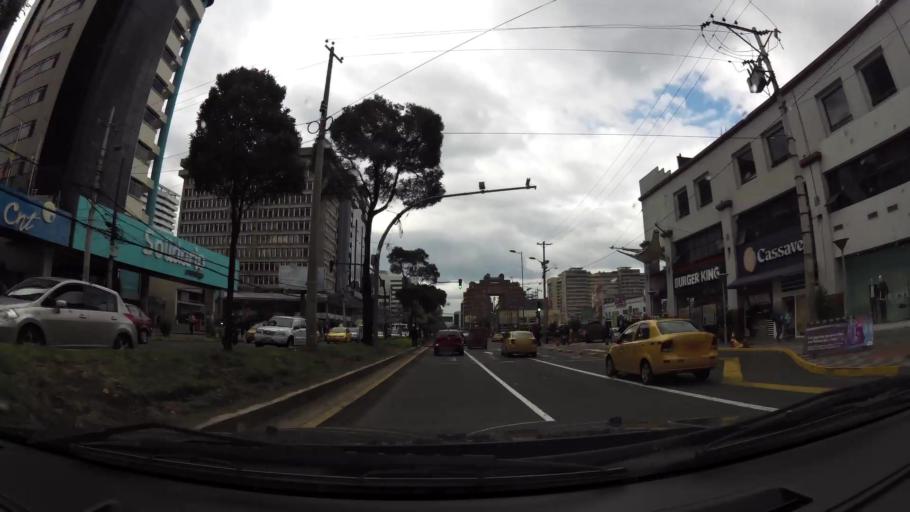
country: EC
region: Pichincha
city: Quito
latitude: -0.1781
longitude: -78.4859
